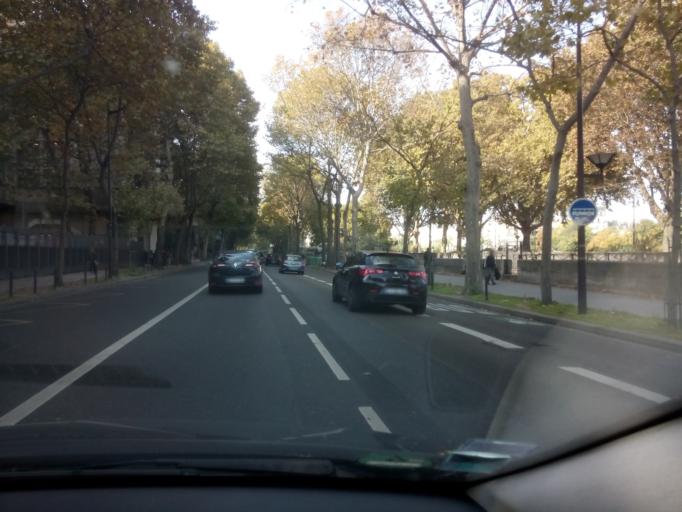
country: FR
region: Ile-de-France
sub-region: Paris
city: Paris
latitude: 48.8472
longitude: 2.3605
